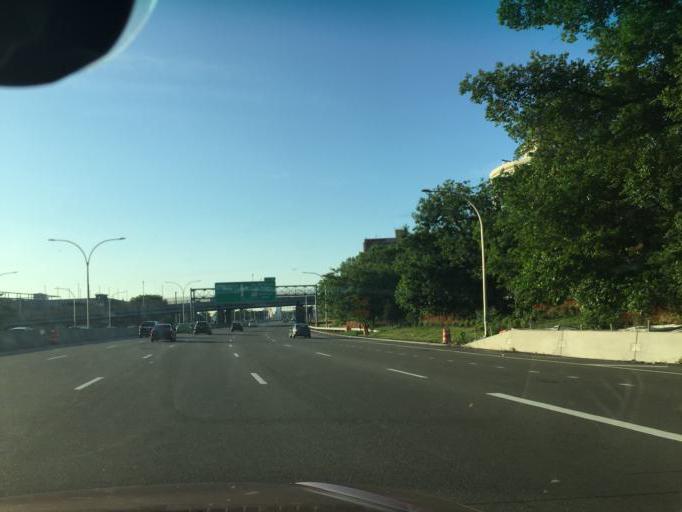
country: US
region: New York
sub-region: Bronx
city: The Bronx
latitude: 40.7710
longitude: -73.8699
